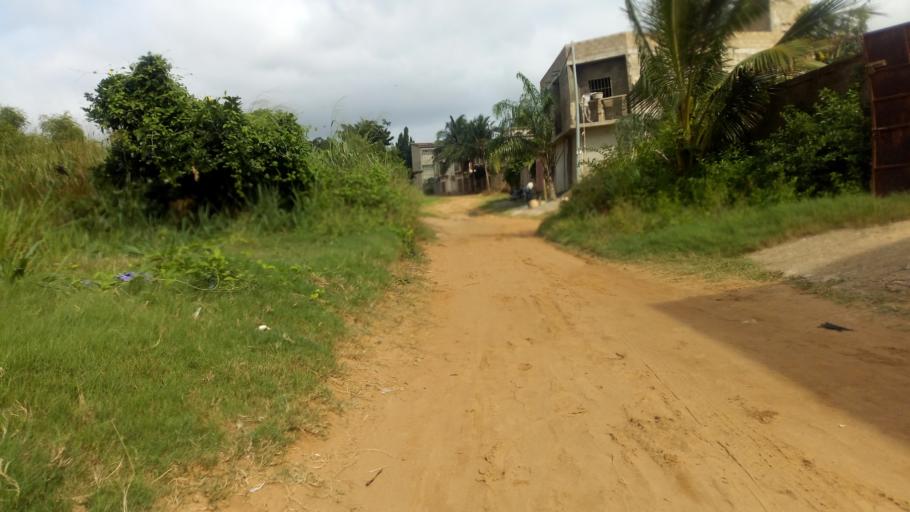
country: TG
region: Maritime
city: Lome
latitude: 6.1741
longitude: 1.1763
